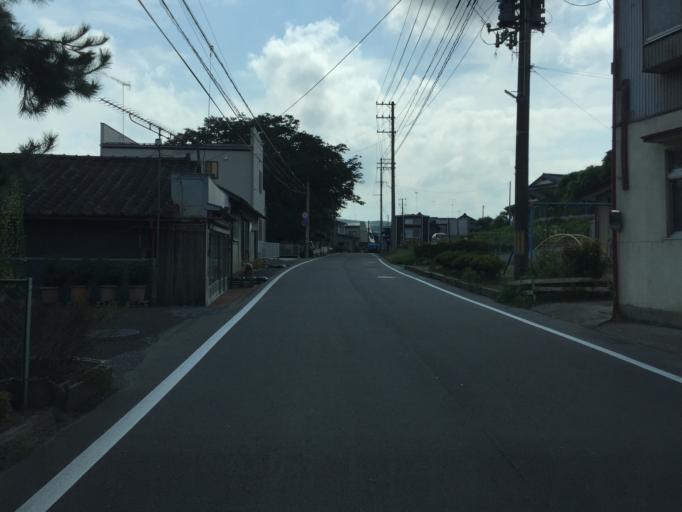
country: JP
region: Fukushima
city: Motomiya
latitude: 37.5227
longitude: 140.4048
